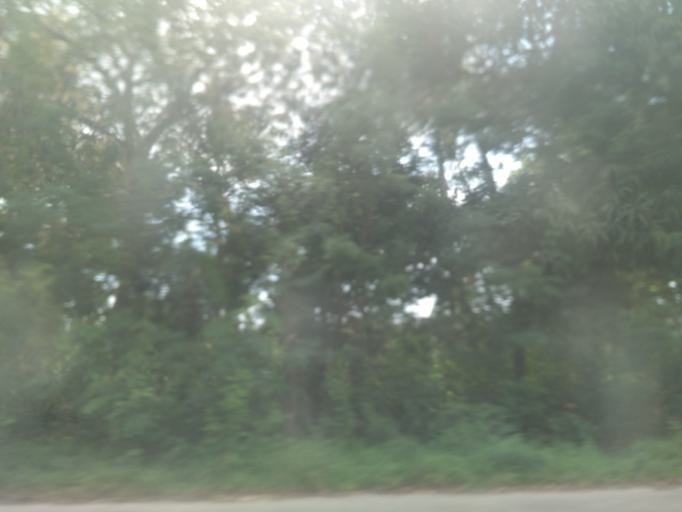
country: TZ
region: Zanzibar Urban/West
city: Zanzibar
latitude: -6.2830
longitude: 39.2809
